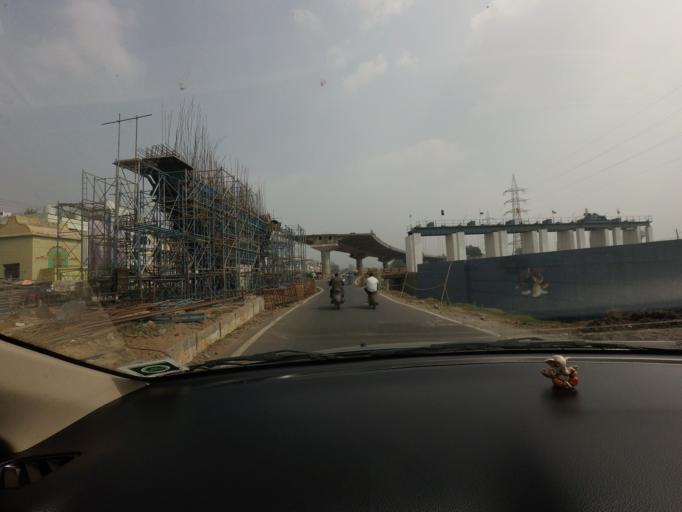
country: IN
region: Andhra Pradesh
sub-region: Krishna
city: Vijayawada
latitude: 16.5122
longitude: 80.6075
